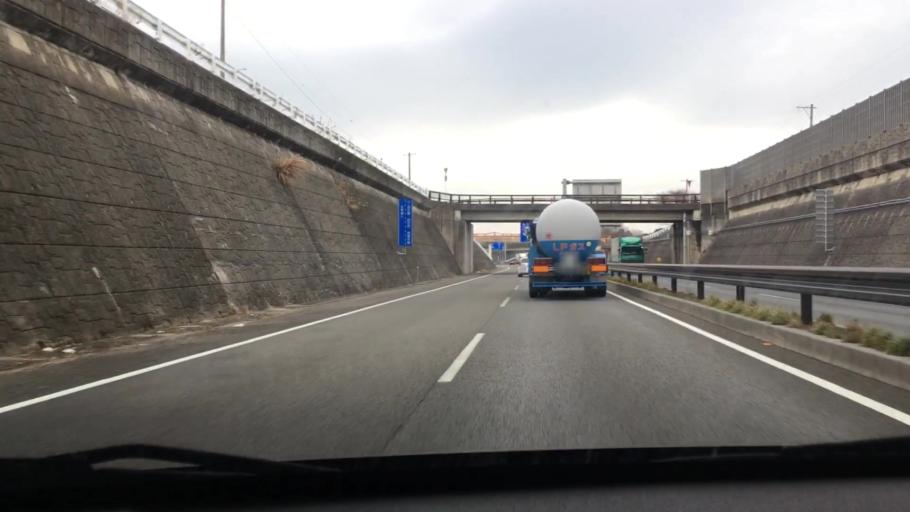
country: JP
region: Mie
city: Kameyama
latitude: 34.8597
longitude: 136.4282
